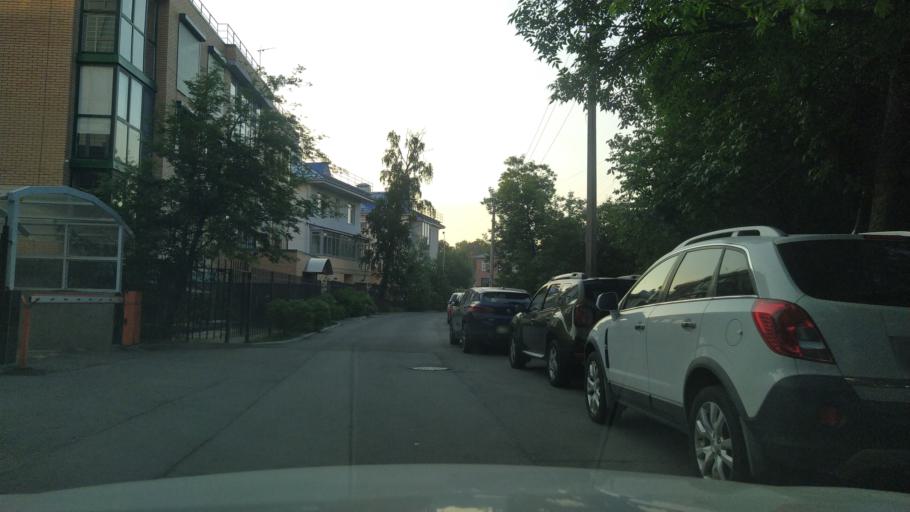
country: RU
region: St.-Petersburg
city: Sestroretsk
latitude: 60.0913
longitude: 29.9483
